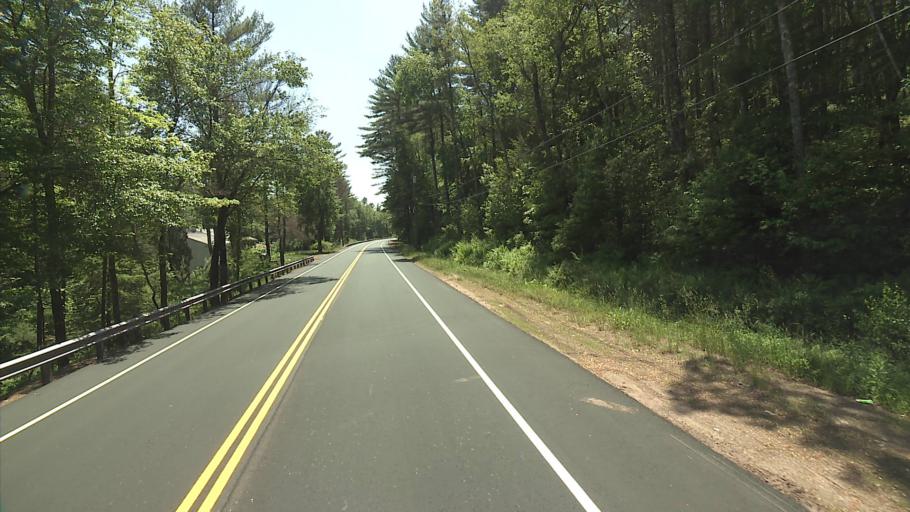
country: US
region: Connecticut
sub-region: Tolland County
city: Crystal Lake
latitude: 41.9619
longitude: -72.3652
